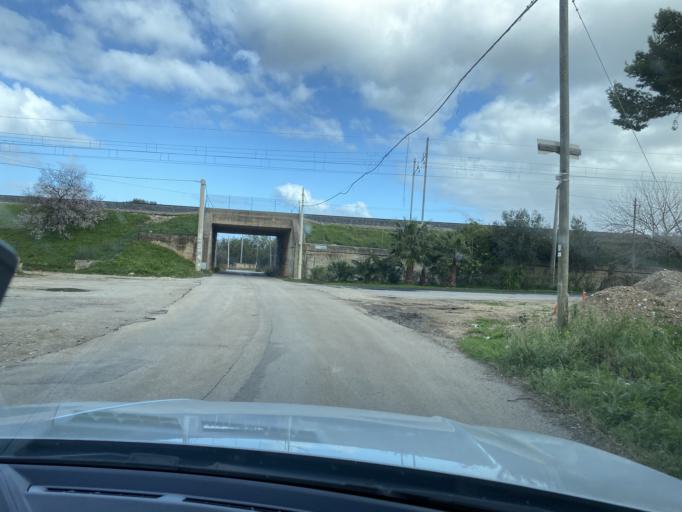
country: IT
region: Sicily
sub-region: Palermo
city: Carini
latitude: 38.1495
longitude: 13.1676
